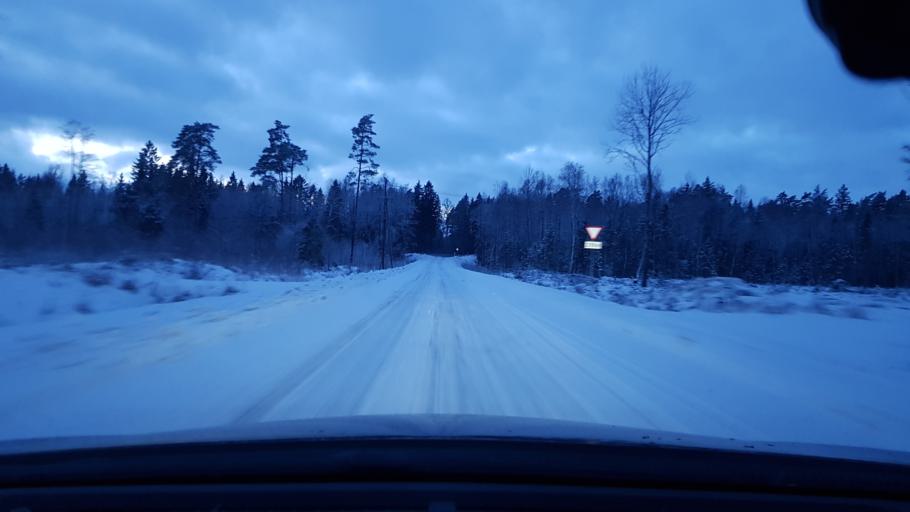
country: EE
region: Harju
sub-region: Nissi vald
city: Turba
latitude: 59.1291
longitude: 24.0755
